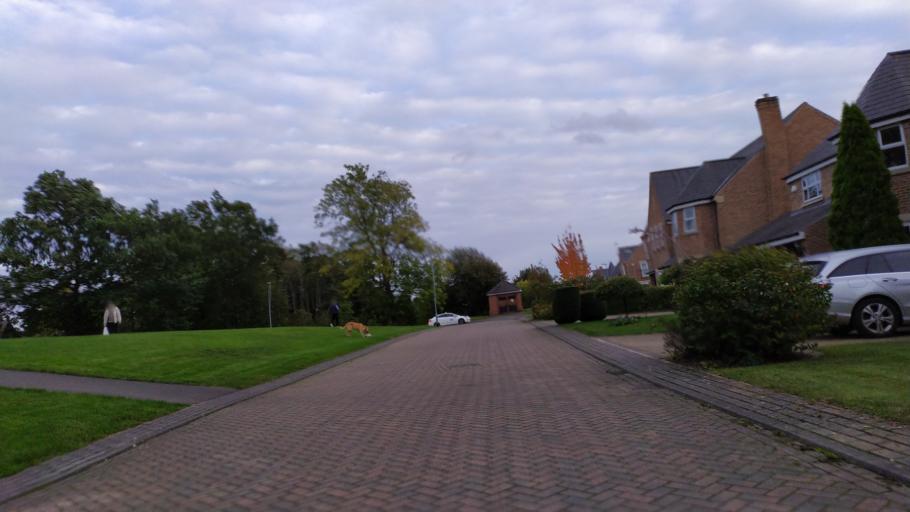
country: GB
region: England
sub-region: City and Borough of Leeds
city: Chapel Allerton
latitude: 53.8314
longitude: -1.5893
